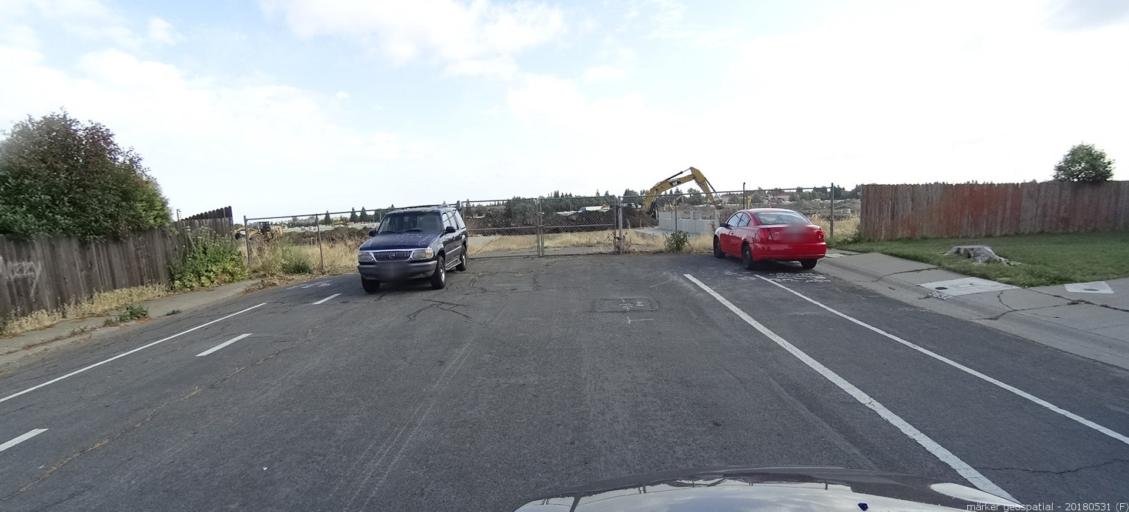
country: US
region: California
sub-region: Sacramento County
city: Sacramento
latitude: 38.6344
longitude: -121.4910
